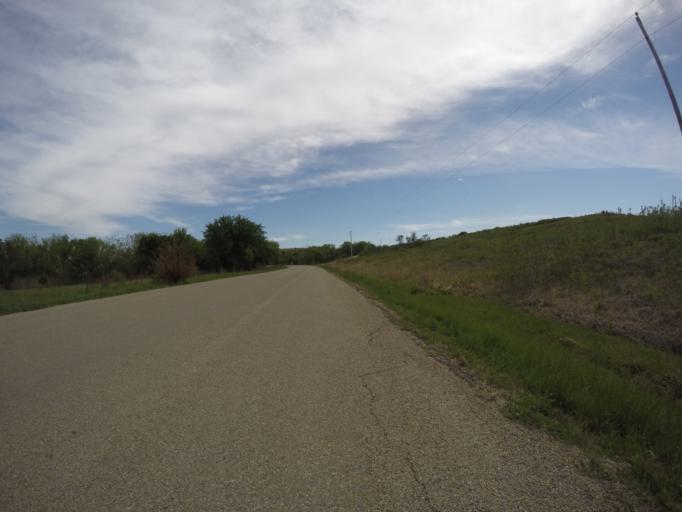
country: US
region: Kansas
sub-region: Riley County
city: Ogden
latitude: 39.0606
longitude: -96.6514
